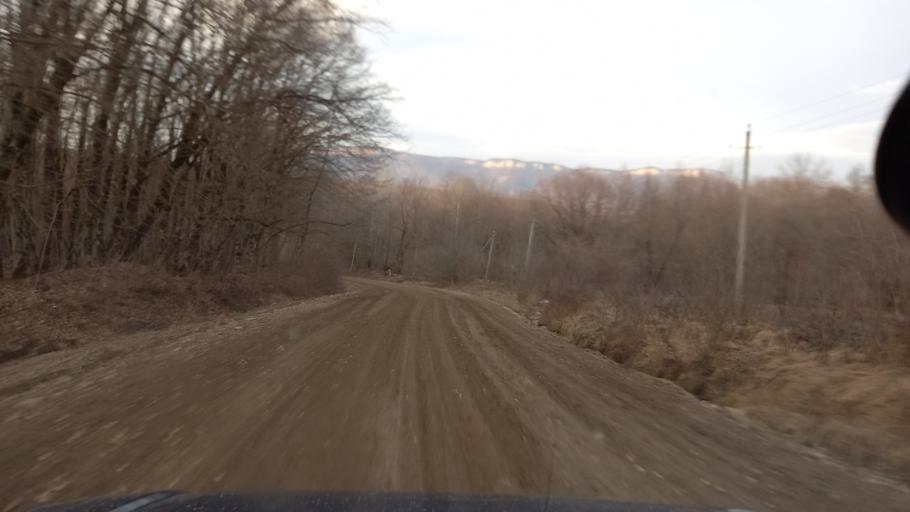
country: RU
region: Adygeya
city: Kamennomostskiy
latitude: 44.1911
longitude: 40.2603
